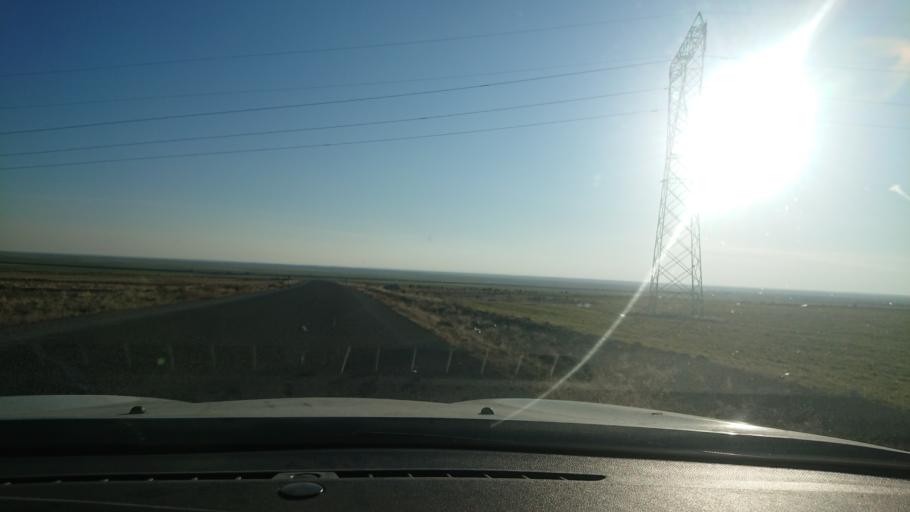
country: TR
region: Aksaray
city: Acipinar
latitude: 38.6728
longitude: 33.7279
